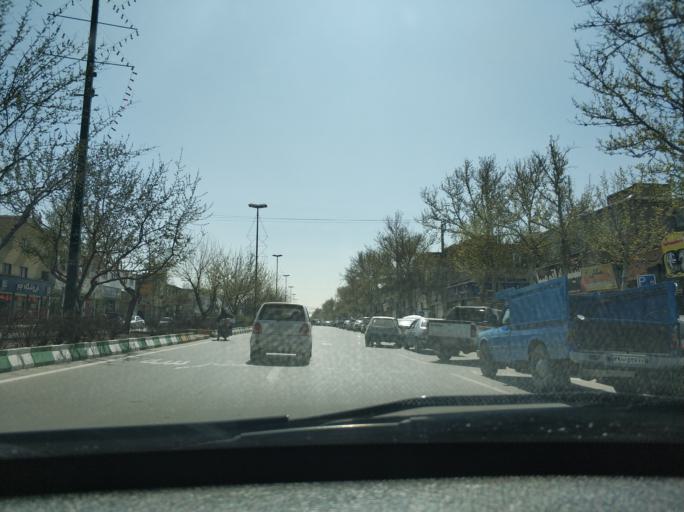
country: IR
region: Razavi Khorasan
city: Mashhad
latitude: 36.2648
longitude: 59.6018
